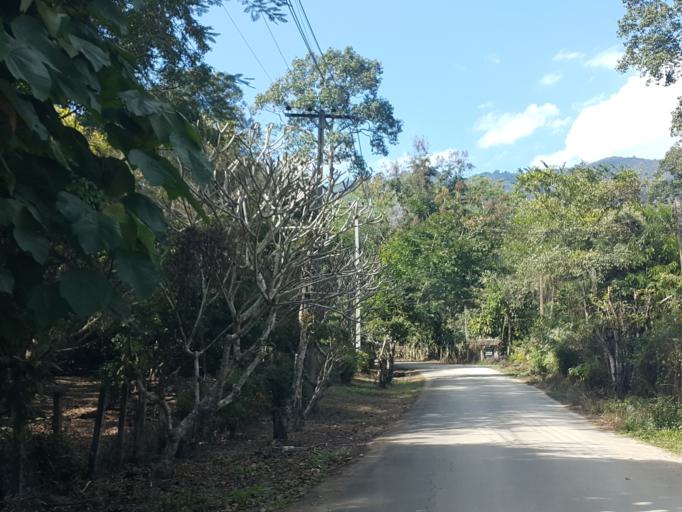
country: TH
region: Chiang Mai
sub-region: Amphoe Chiang Dao
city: Chiang Dao
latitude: 19.4028
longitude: 98.9261
